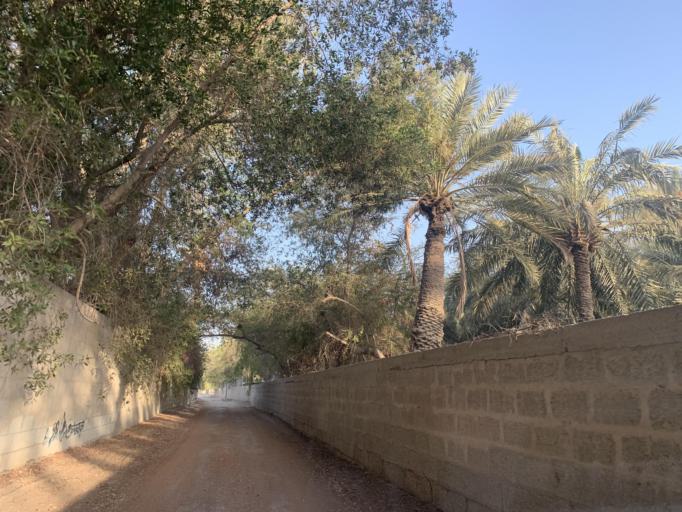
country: BH
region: Manama
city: Jidd Hafs
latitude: 26.2211
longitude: 50.5286
